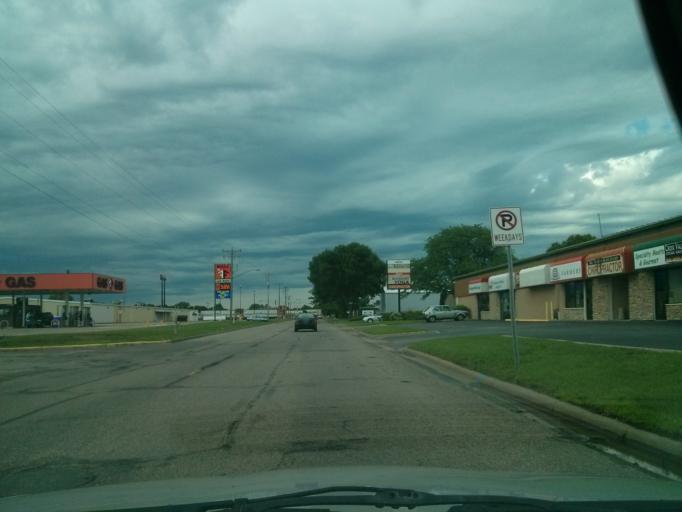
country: US
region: Wisconsin
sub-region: Saint Croix County
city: Hudson
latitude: 44.9596
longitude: -92.7341
